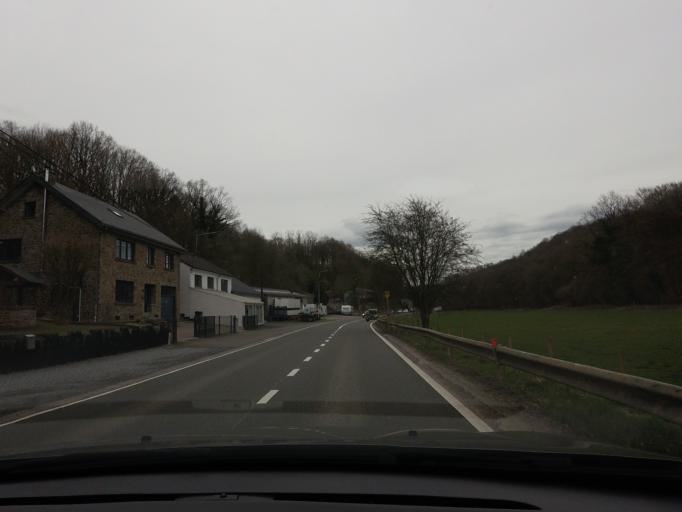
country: BE
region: Wallonia
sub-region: Province de Liege
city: Aywaille
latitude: 50.4566
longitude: 5.6733
